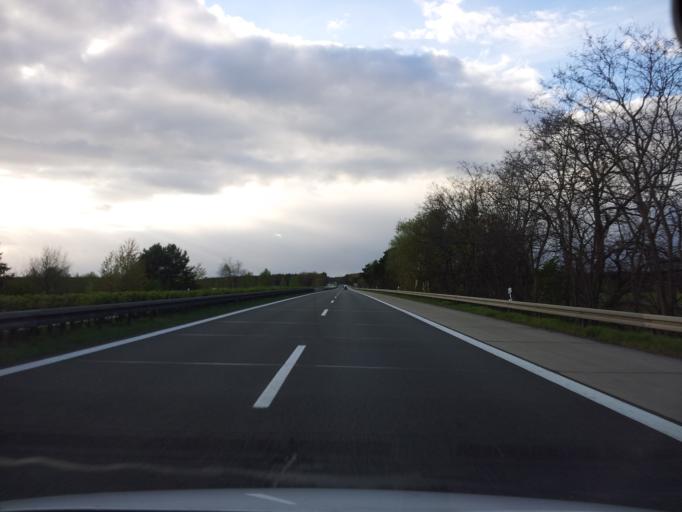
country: DE
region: Brandenburg
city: Vetschau
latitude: 51.8129
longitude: 14.0253
